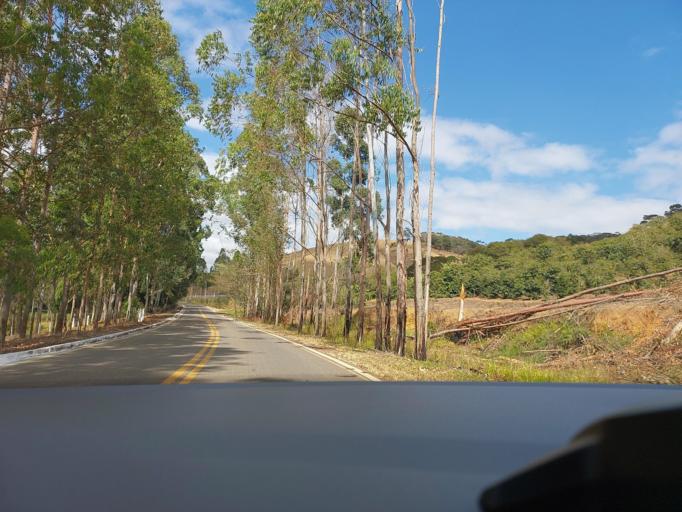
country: BR
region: Minas Gerais
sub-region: Visconde Do Rio Branco
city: Visconde do Rio Branco
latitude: -20.9200
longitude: -42.6386
